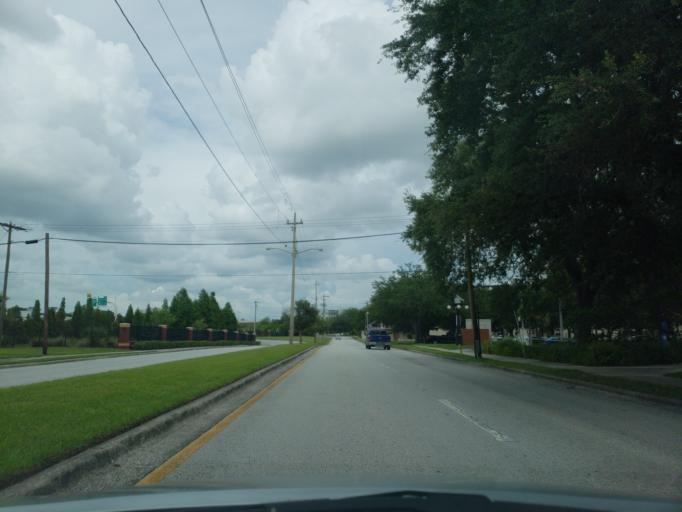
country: US
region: Florida
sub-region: Hillsborough County
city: Tampa
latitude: 27.9633
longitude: -82.4458
